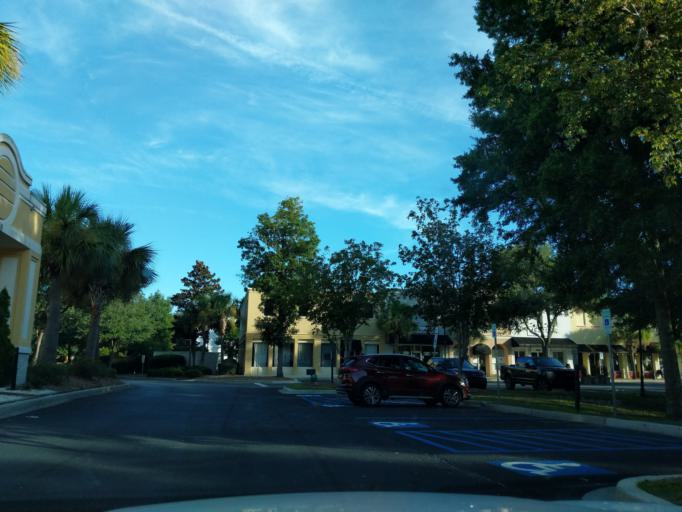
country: US
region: South Carolina
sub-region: Charleston County
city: Isle of Palms
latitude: 32.8296
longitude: -79.8239
